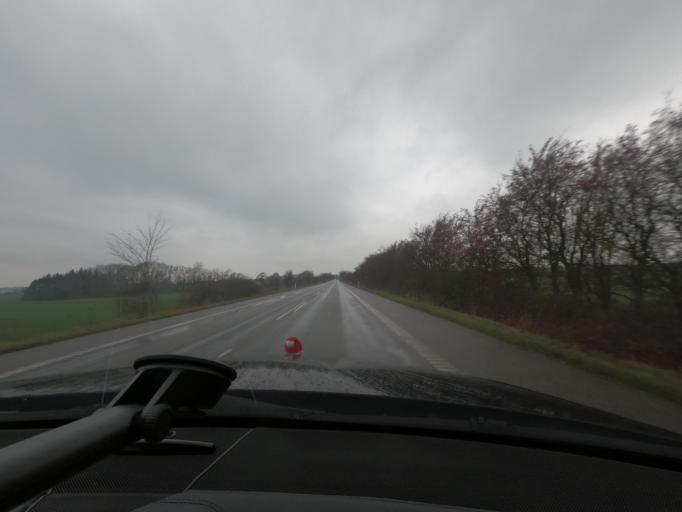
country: DK
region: South Denmark
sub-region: Sonderborg Kommune
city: Horuphav
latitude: 54.8862
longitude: 9.9828
